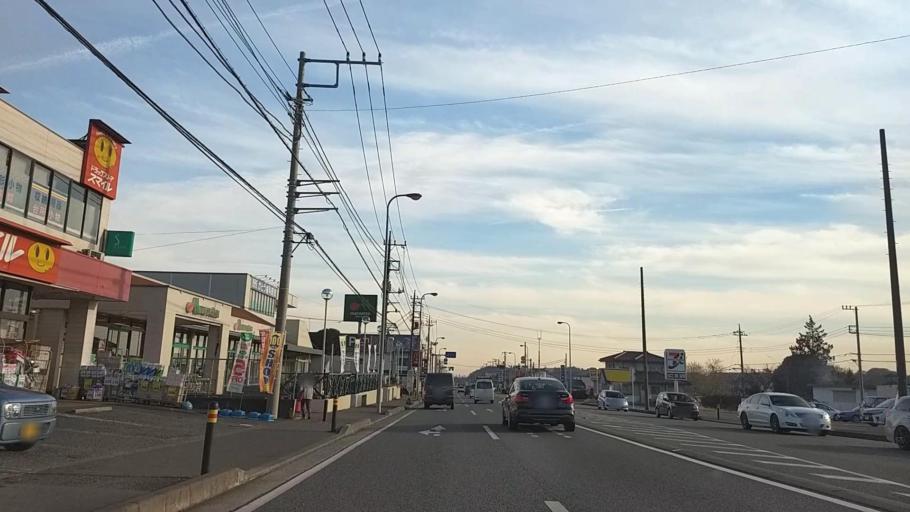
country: JP
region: Kanagawa
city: Atsugi
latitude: 35.4905
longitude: 139.3228
